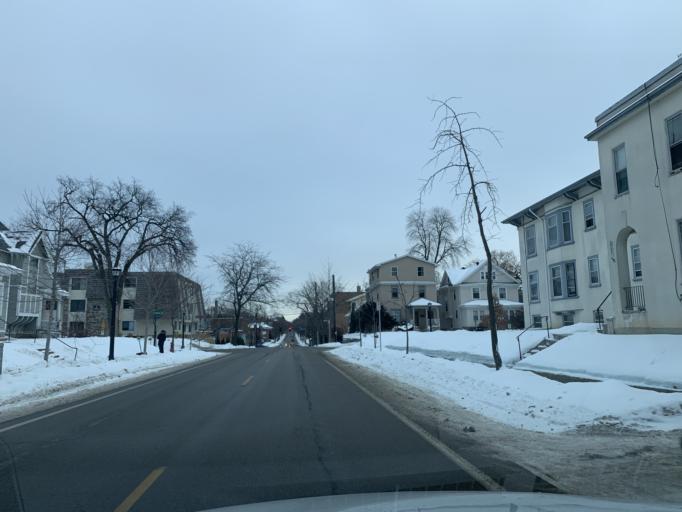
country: US
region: Minnesota
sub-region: Hennepin County
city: Minneapolis
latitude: 44.9591
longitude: -93.2900
